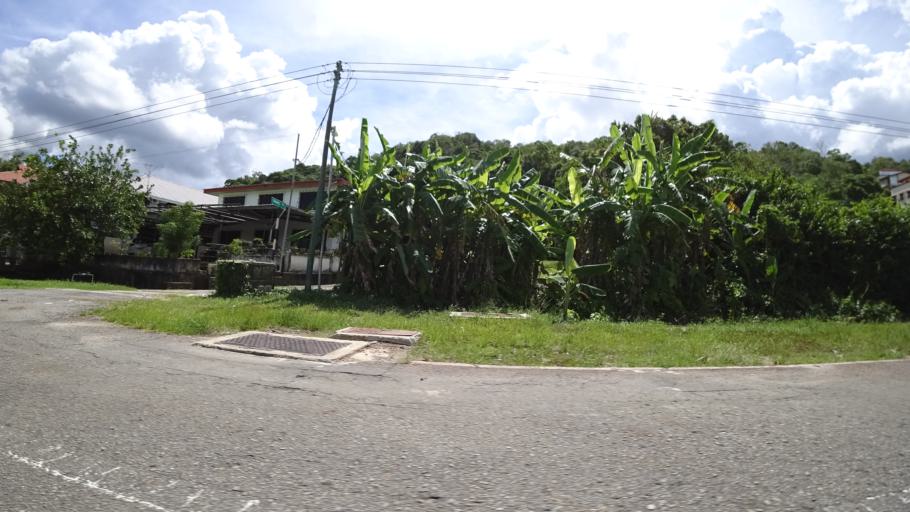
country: BN
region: Brunei and Muara
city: Bandar Seri Begawan
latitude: 4.8896
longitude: 114.9758
